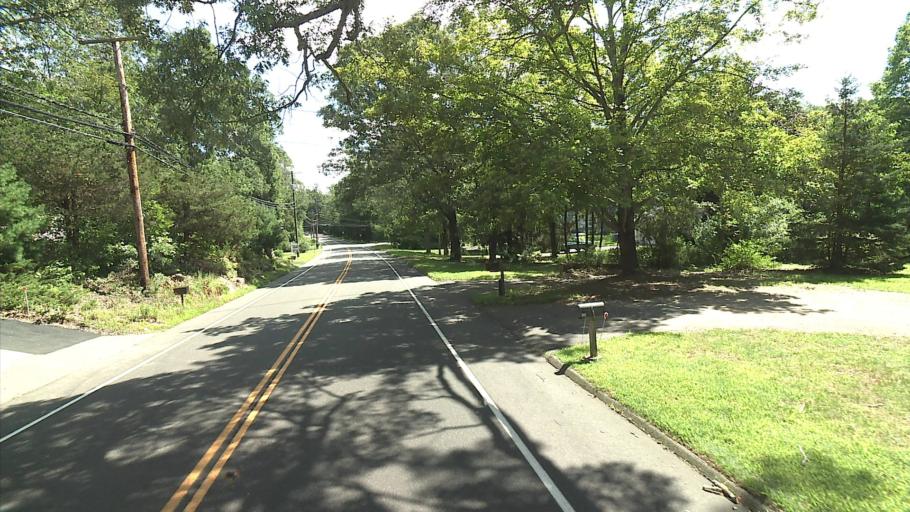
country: US
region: Connecticut
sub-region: New London County
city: Niantic
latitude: 41.3591
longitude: -72.2474
